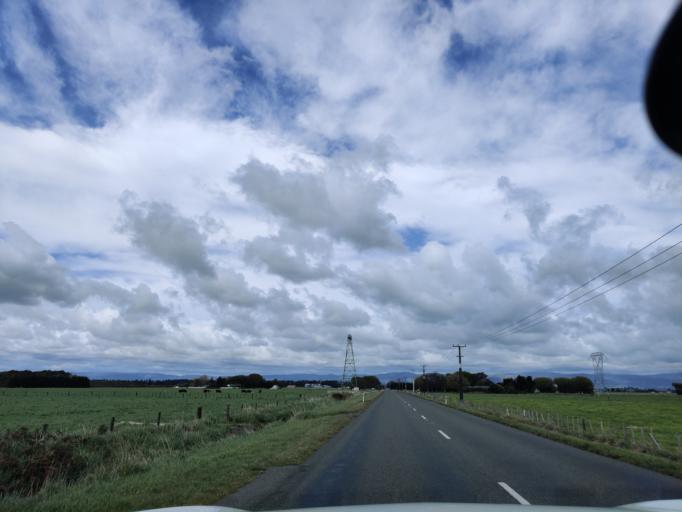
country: NZ
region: Manawatu-Wanganui
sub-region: Palmerston North City
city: Palmerston North
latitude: -40.3305
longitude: 175.5113
